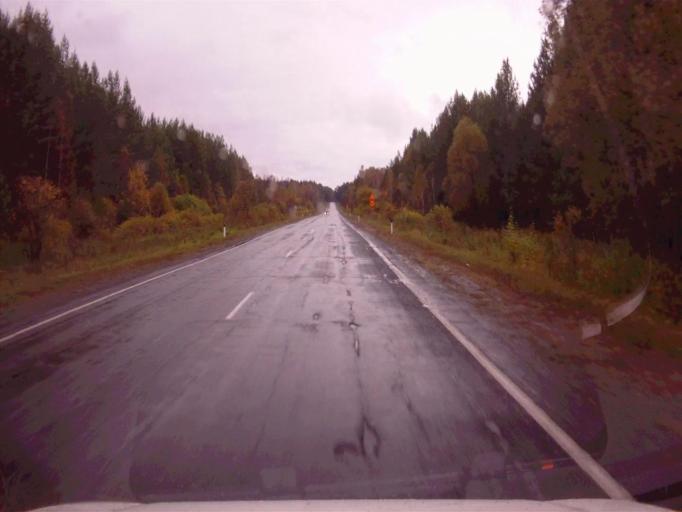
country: RU
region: Chelyabinsk
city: Verkhniy Ufaley
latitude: 56.0154
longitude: 60.3104
